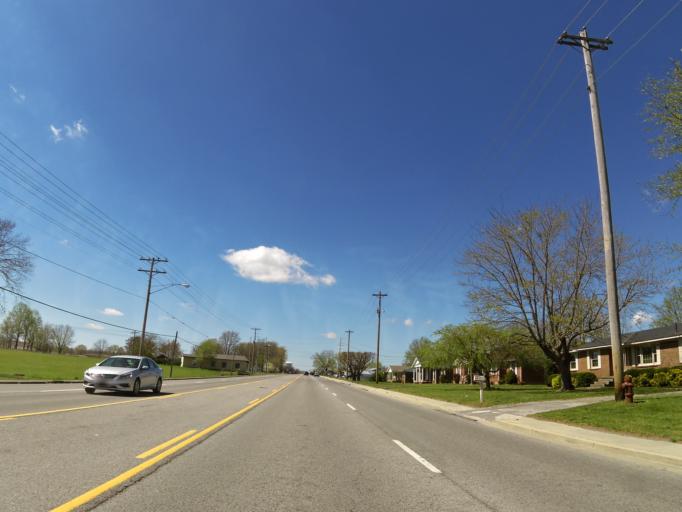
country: US
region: Tennessee
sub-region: DeKalb County
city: Smithville
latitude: 35.9621
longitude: -85.8425
